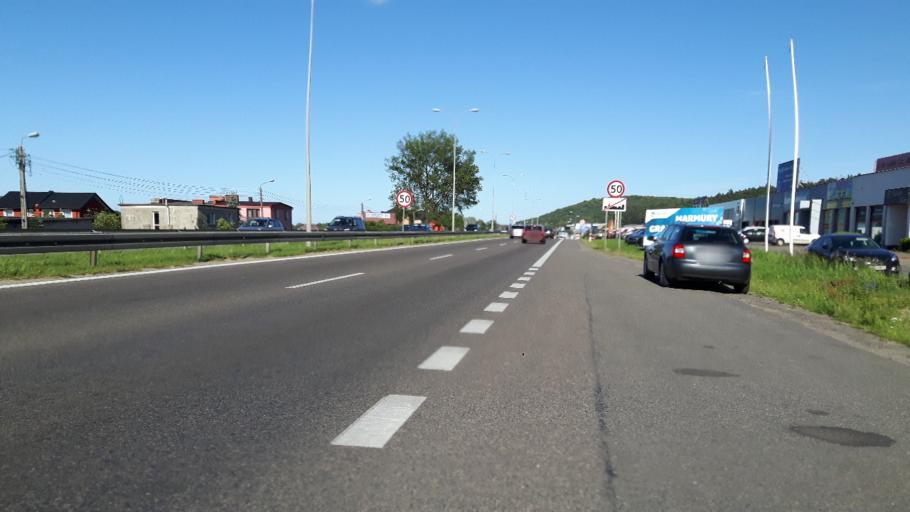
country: PL
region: Pomeranian Voivodeship
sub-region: Powiat wejherowski
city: Reda
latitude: 54.6030
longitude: 18.2942
